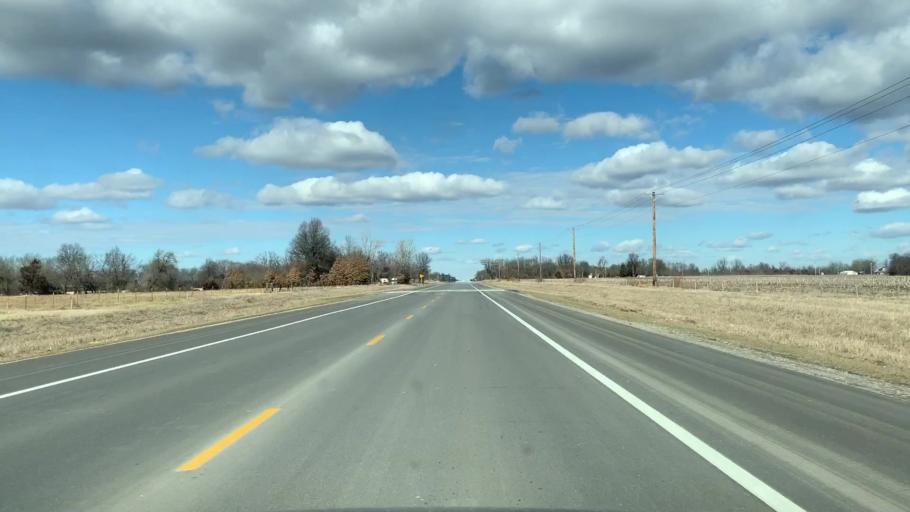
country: US
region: Kansas
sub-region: Cherokee County
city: Columbus
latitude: 37.2167
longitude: -94.8318
